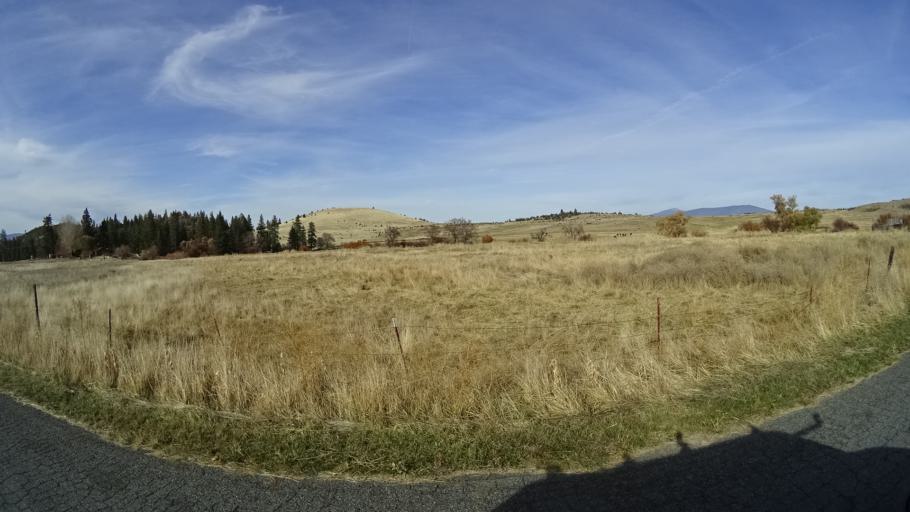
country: US
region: California
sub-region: Siskiyou County
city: Weed
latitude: 41.4650
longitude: -122.3995
